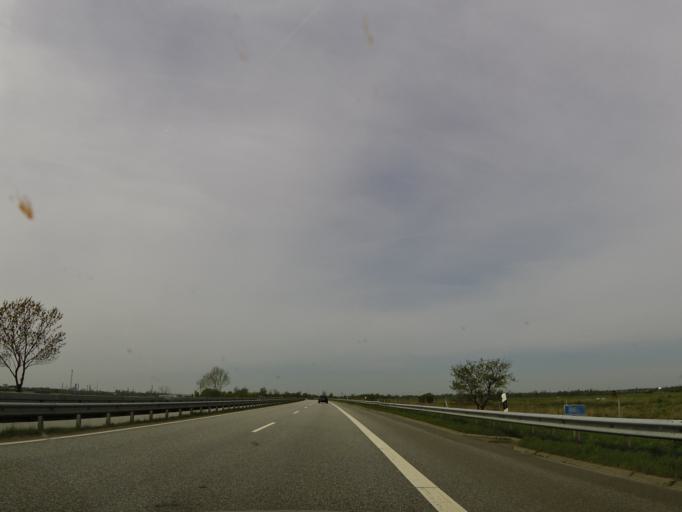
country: DE
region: Schleswig-Holstein
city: Nordhastedt
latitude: 54.1670
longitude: 9.1398
